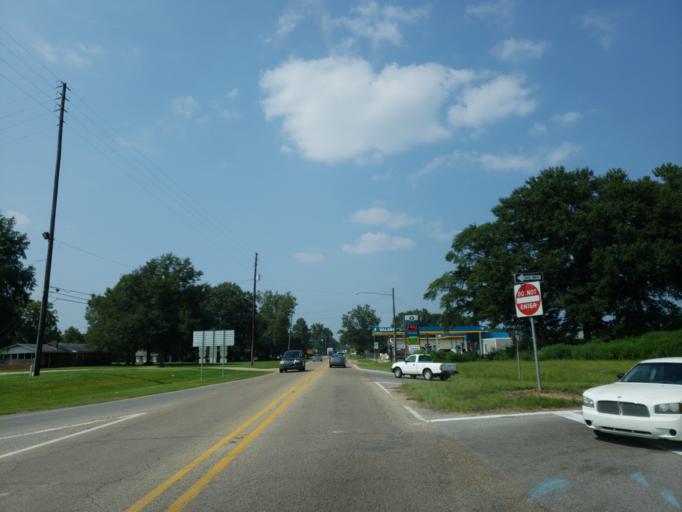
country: US
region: Mississippi
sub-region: Jones County
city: Ellisville
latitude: 31.6343
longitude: -89.1809
